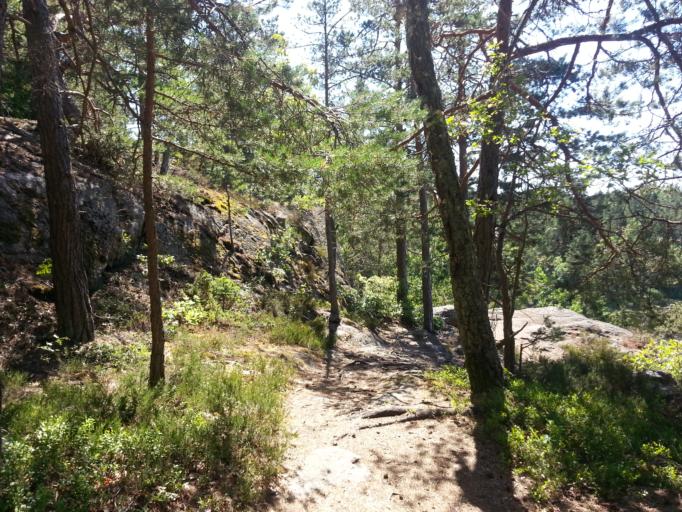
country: SE
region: Stockholm
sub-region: Tyreso Kommun
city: Bollmora
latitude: 59.2212
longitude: 18.2707
